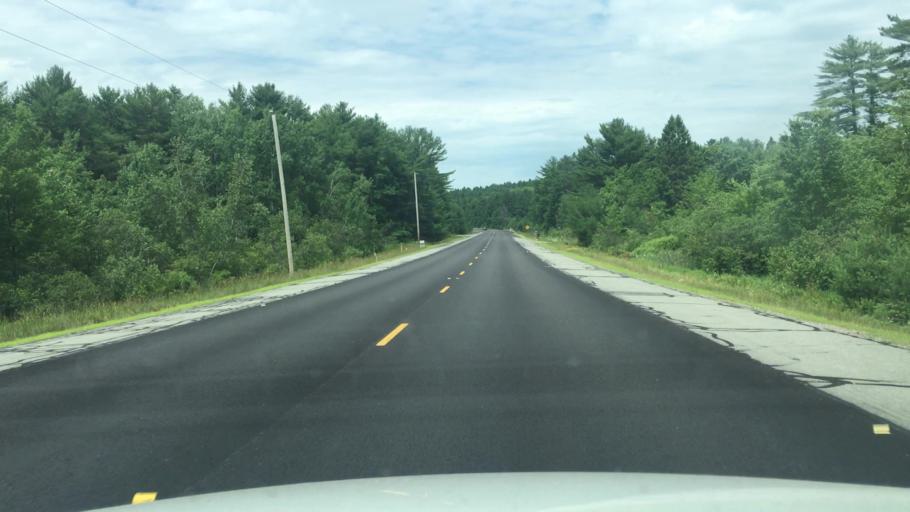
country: US
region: Maine
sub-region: Waldo County
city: Palermo
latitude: 44.4041
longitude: -69.4786
